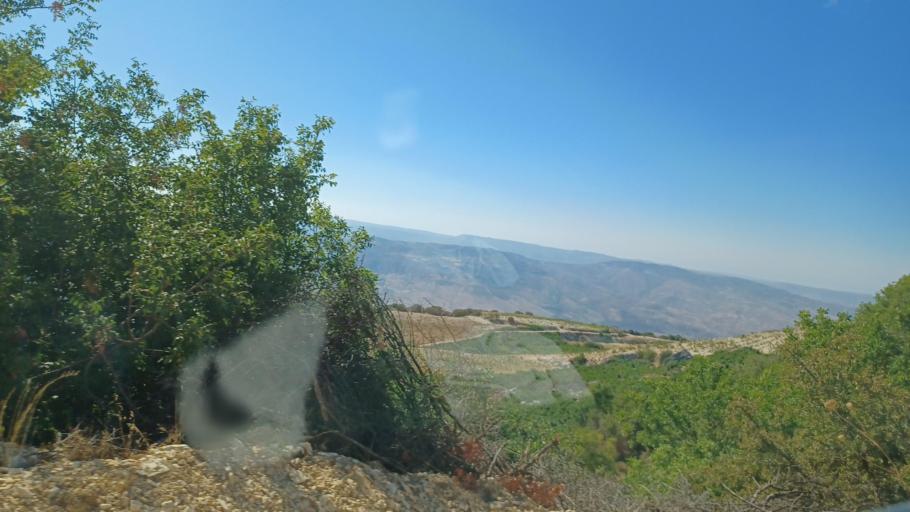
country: CY
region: Limassol
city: Pachna
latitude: 34.9044
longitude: 32.6367
